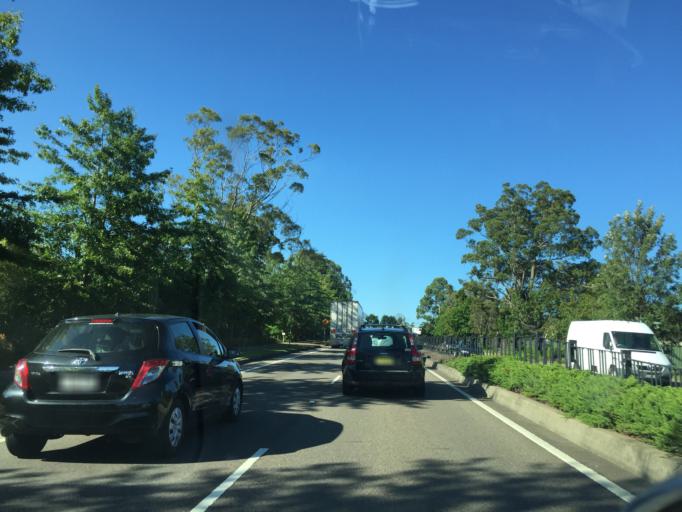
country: AU
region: New South Wales
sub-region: Blue Mountains Municipality
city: Blaxland
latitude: -33.6938
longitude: 150.5413
